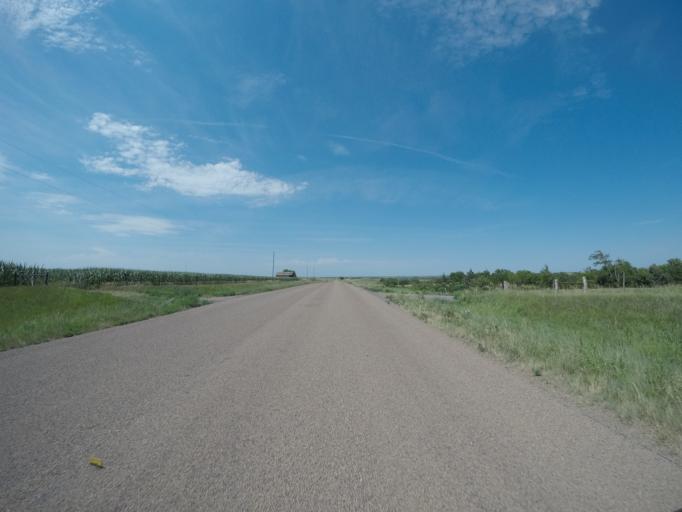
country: US
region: Nebraska
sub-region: Webster County
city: Red Cloud
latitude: 40.0292
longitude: -98.3303
